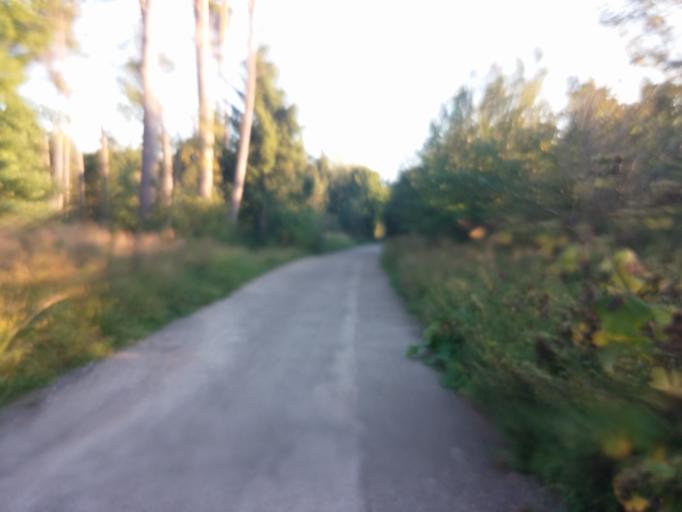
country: DE
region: Bavaria
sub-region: Upper Bavaria
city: Neubiberg
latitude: 48.1049
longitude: 11.6857
